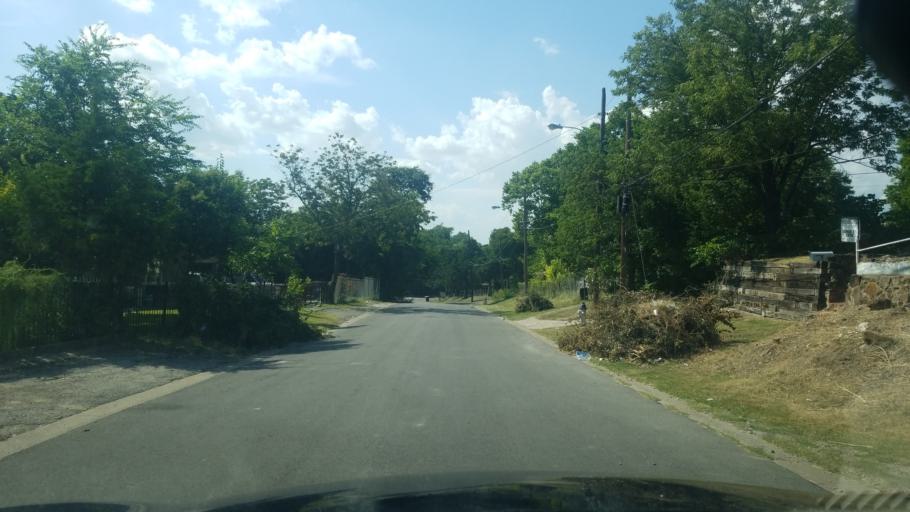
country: US
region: Texas
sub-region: Dallas County
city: Dallas
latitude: 32.7252
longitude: -96.8077
